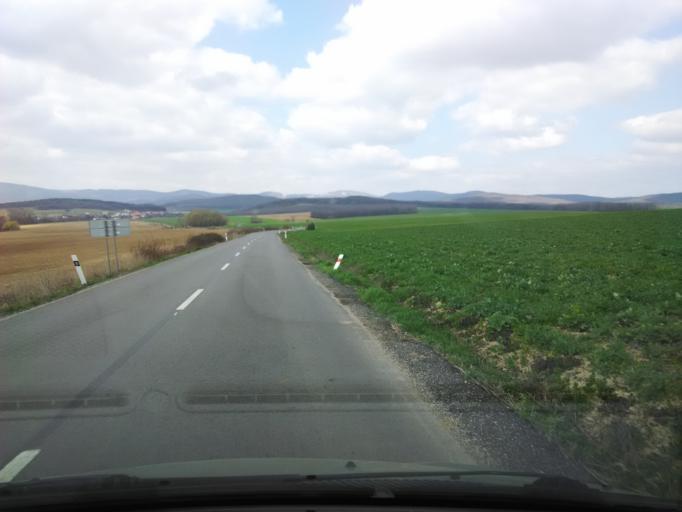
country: SK
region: Nitriansky
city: Zlate Moravce
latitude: 48.4147
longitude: 18.3410
